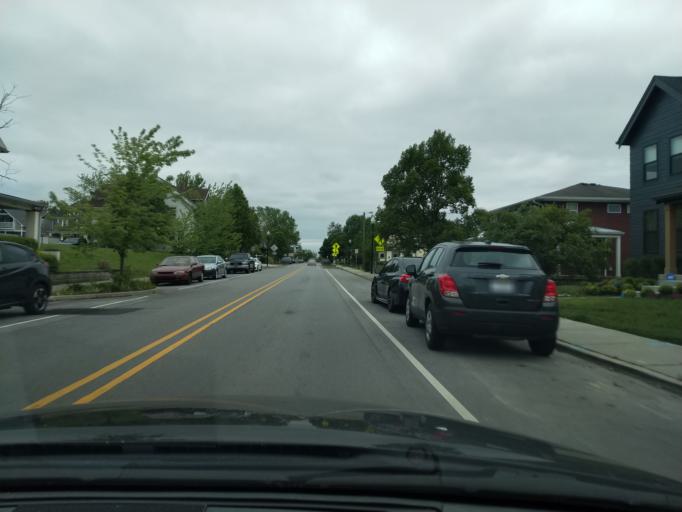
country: US
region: Indiana
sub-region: Marion County
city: Indianapolis
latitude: 39.8002
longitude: -86.1496
